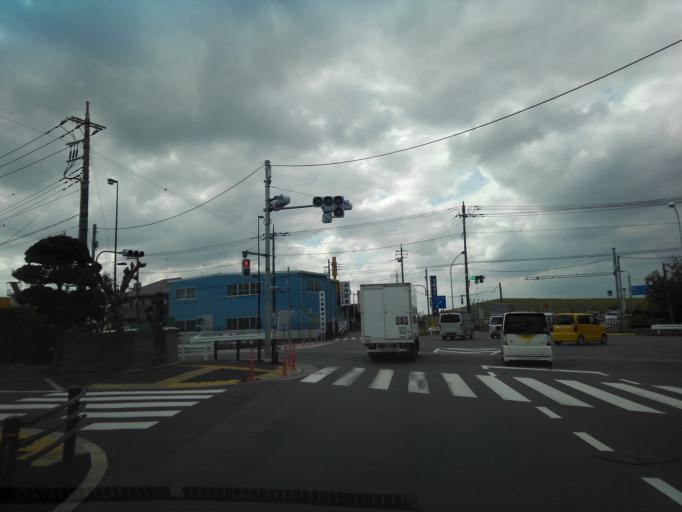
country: JP
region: Tokyo
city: Fussa
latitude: 35.7690
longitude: 139.3475
